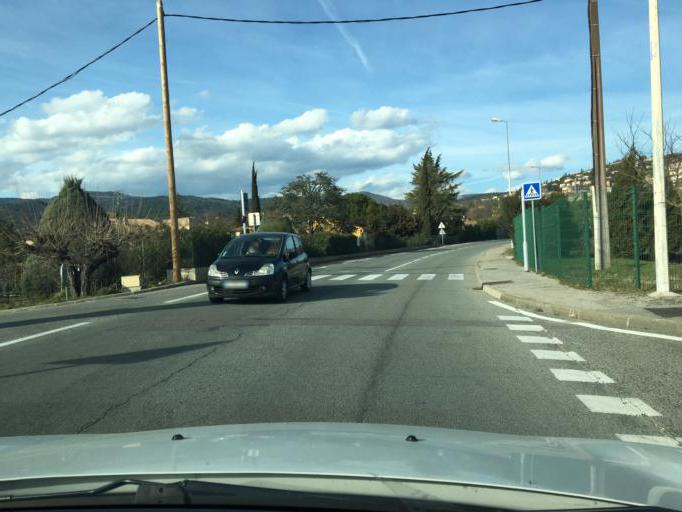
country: FR
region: Provence-Alpes-Cote d'Azur
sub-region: Departement du Var
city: Fayence
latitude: 43.6159
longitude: 6.6874
